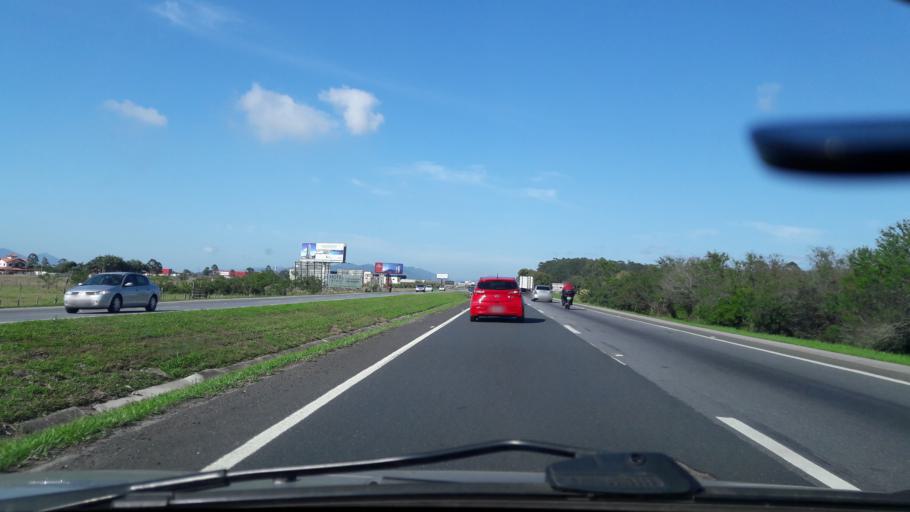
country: BR
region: Santa Catarina
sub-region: Tijucas
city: Tijucas
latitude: -27.2071
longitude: -48.6192
